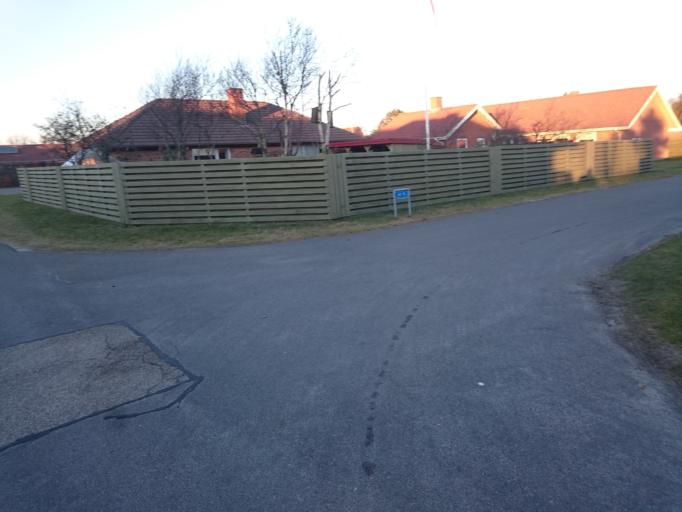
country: DK
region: South Denmark
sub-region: Fano Kommune
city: Nordby
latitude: 55.4436
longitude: 8.3934
